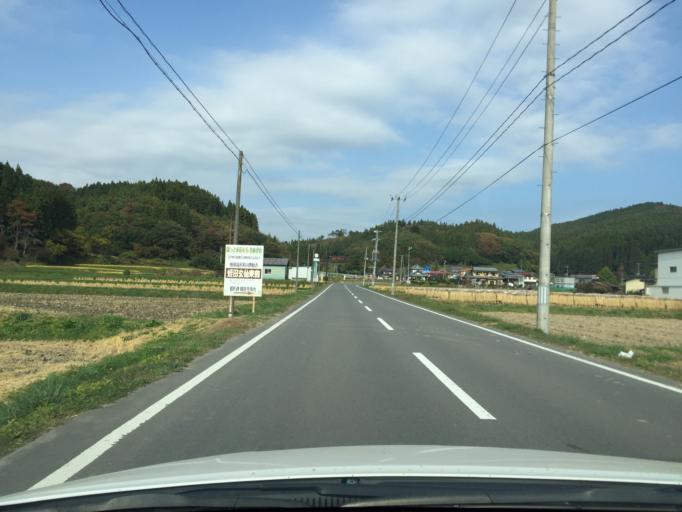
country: JP
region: Fukushima
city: Ishikawa
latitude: 36.9856
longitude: 140.4838
